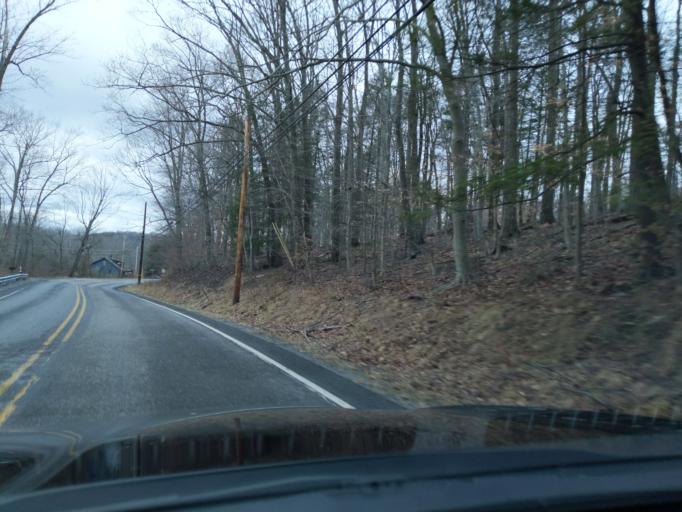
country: US
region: Pennsylvania
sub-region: Blair County
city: Bellwood
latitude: 40.5826
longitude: -78.3421
